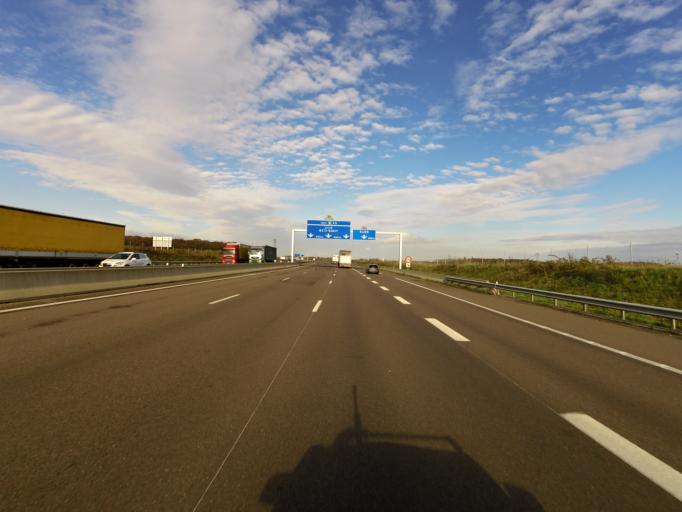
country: FR
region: Bourgogne
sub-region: Departement de la Cote-d'Or
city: Perrigny-les-Dijon
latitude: 47.2325
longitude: 5.0200
